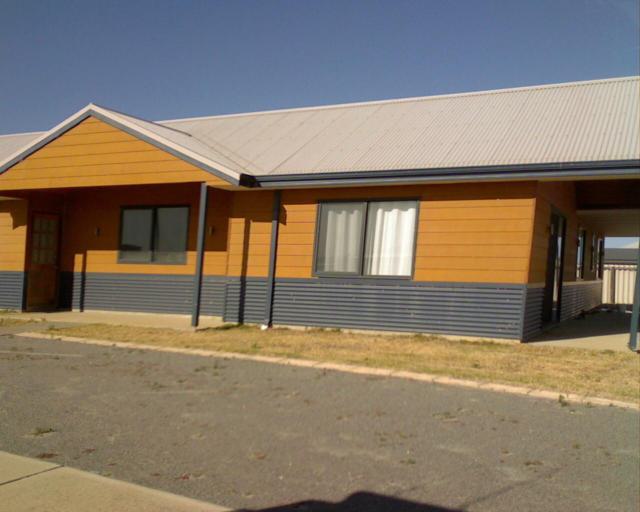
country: AU
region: Western Australia
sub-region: Dandaragan
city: Jurien Bay
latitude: -30.0686
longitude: 114.9750
